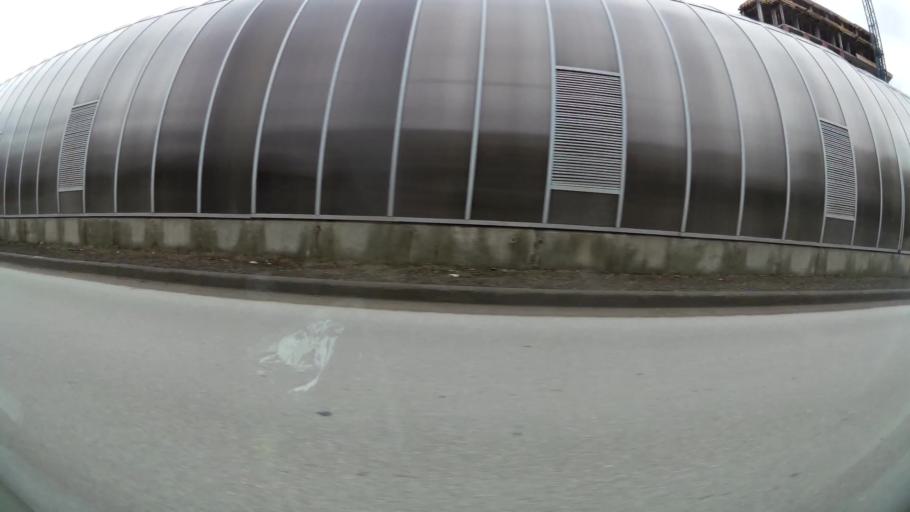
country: BG
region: Sofia-Capital
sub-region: Stolichna Obshtina
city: Sofia
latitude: 42.7385
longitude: 23.2892
